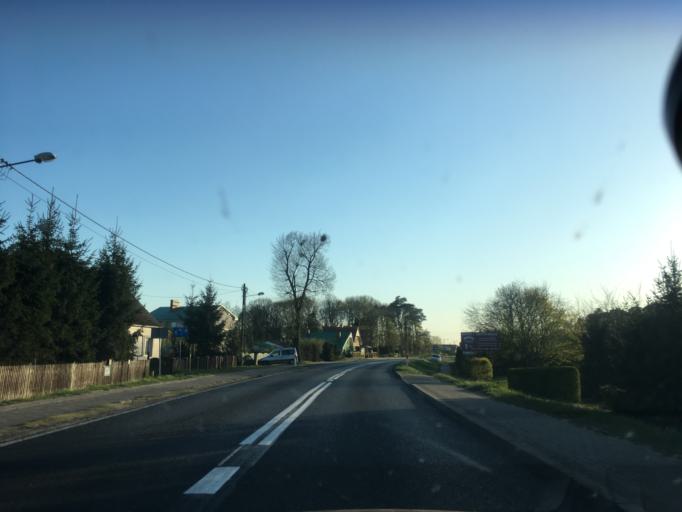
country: PL
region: Lubusz
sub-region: Powiat gorzowski
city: Jenin
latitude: 52.6952
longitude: 15.0938
